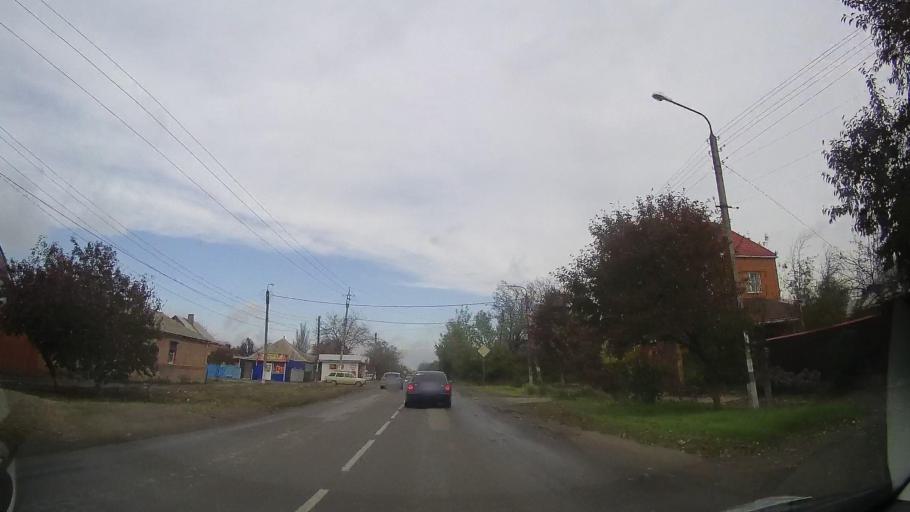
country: RU
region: Rostov
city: Bataysk
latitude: 47.1424
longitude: 39.7671
